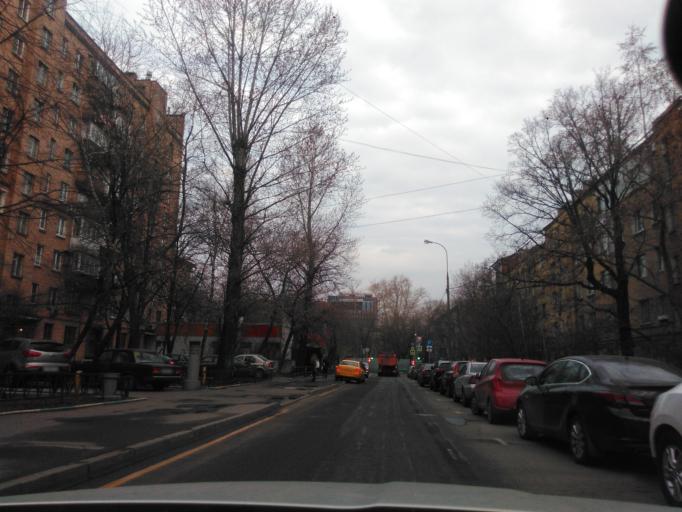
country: RU
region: Moskovskaya
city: Dorogomilovo
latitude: 55.7864
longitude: 37.5732
